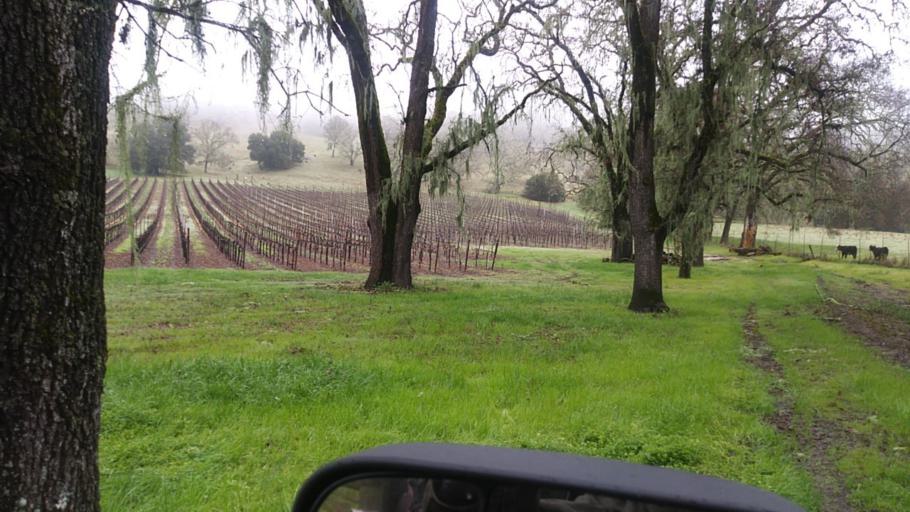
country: US
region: California
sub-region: Sonoma County
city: Cloverdale
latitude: 38.9548
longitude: -123.0487
